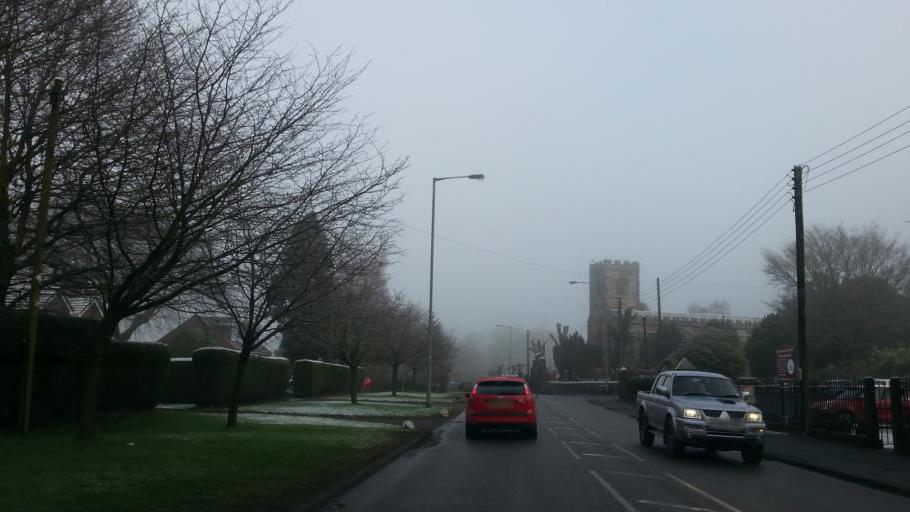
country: GB
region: England
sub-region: Staffordshire
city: Biddulph
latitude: 53.1274
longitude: -2.1668
